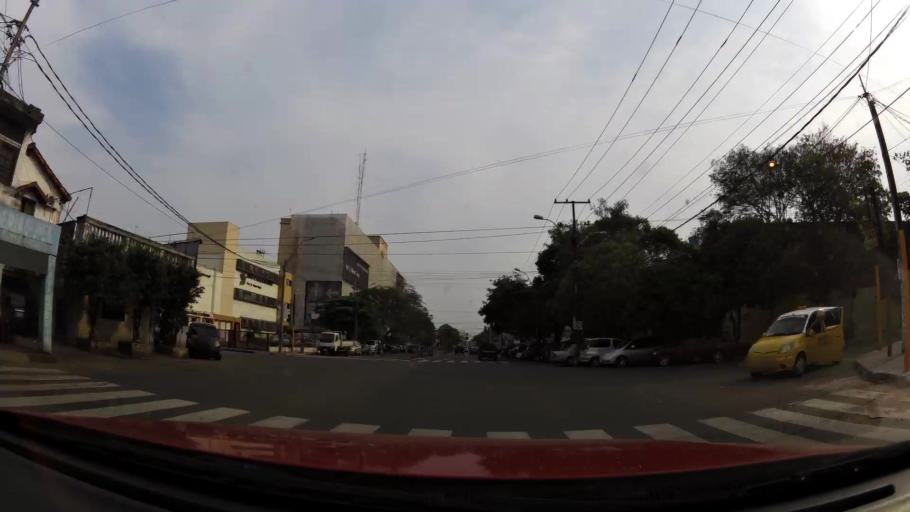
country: PY
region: Asuncion
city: Asuncion
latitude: -25.2996
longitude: -57.6129
